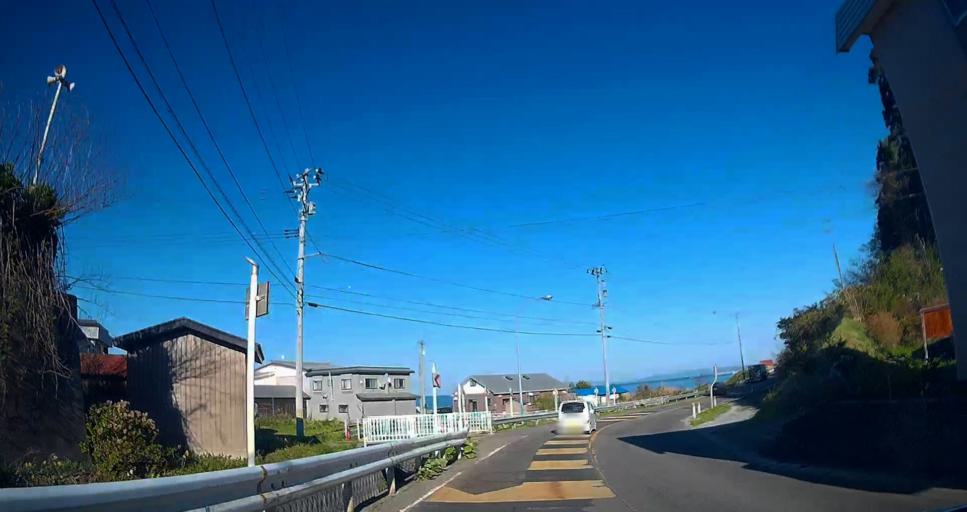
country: JP
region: Aomori
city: Mutsu
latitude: 41.4218
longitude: 141.1503
